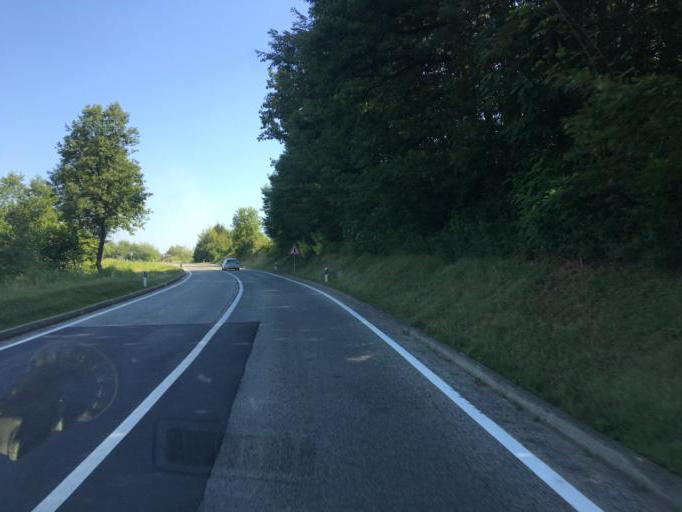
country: HR
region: Karlovacka
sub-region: Grad Karlovac
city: Slunj
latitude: 45.2246
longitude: 15.5585
